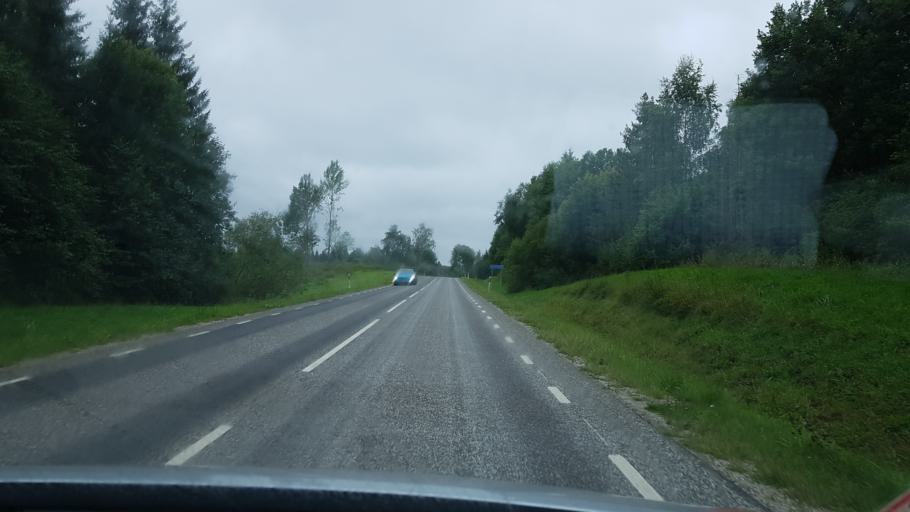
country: EE
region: Vorumaa
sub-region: Antsla vald
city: Vana-Antsla
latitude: 58.0050
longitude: 26.6442
